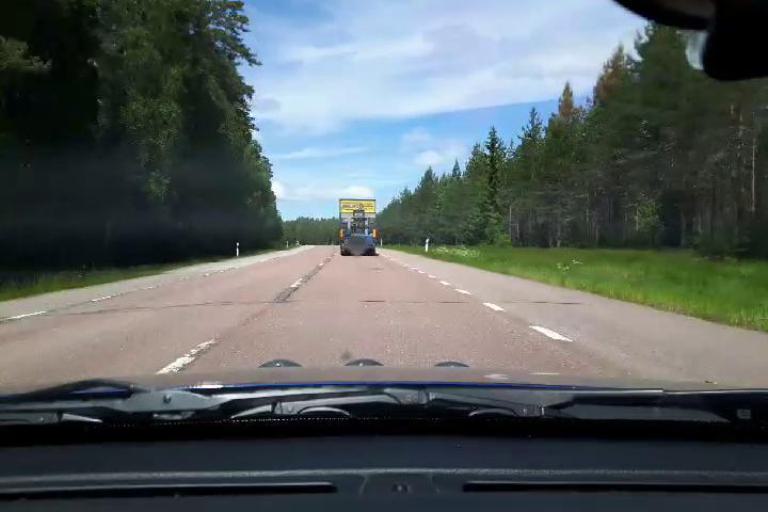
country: SE
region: Uppsala
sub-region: Osthammars Kommun
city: Bjorklinge
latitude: 60.1283
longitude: 17.5096
